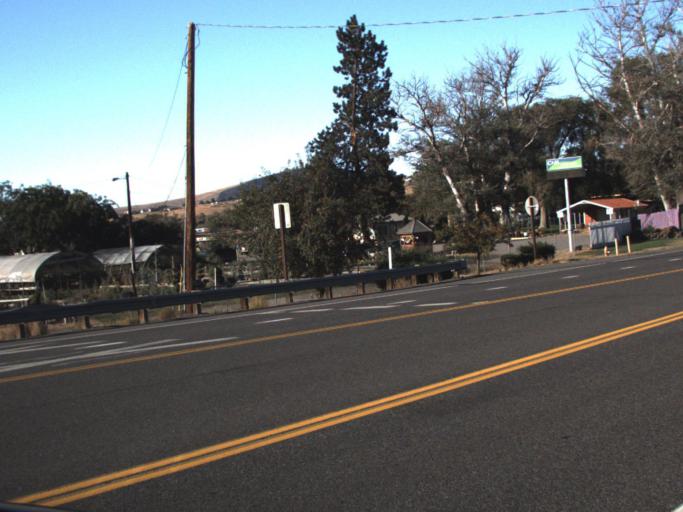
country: US
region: Washington
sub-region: Benton County
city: Richland
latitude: 46.2931
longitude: -119.3072
